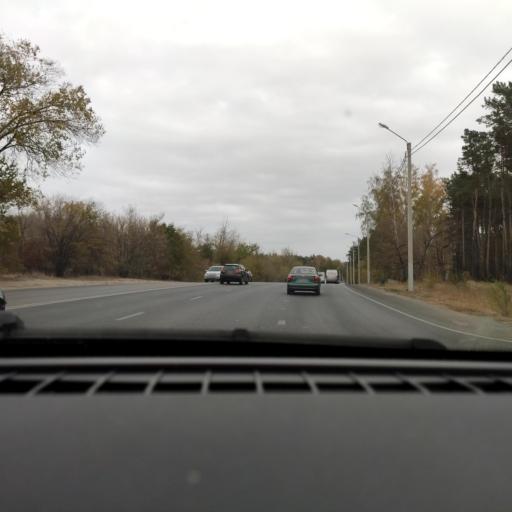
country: RU
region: Voronezj
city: Voronezh
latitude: 51.6802
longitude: 39.2743
